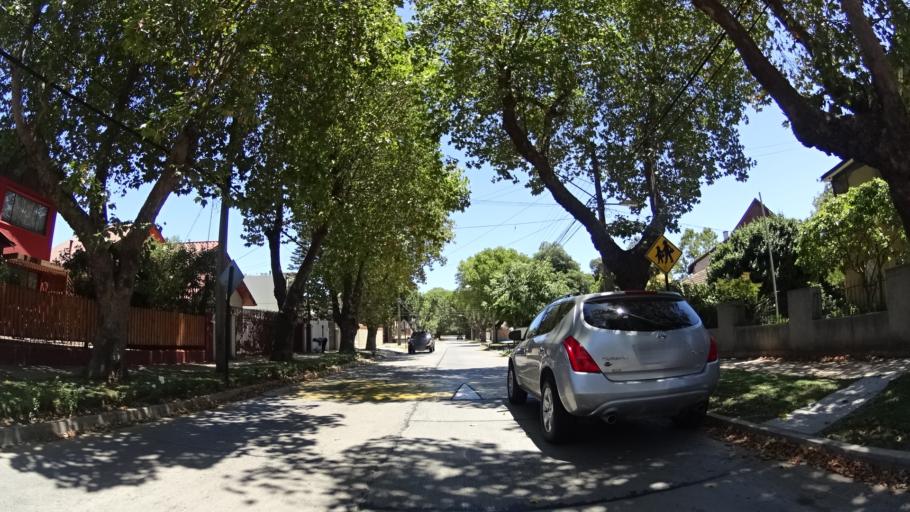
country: CL
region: Valparaiso
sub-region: Provincia de Valparaiso
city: Vina del Mar
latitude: -33.0288
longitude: -71.5326
